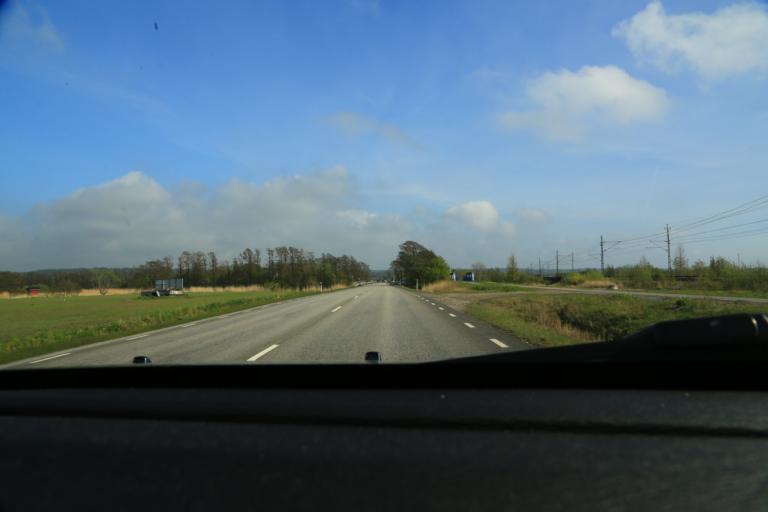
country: SE
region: Halland
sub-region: Kungsbacka Kommun
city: Frillesas
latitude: 57.2292
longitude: 12.2107
